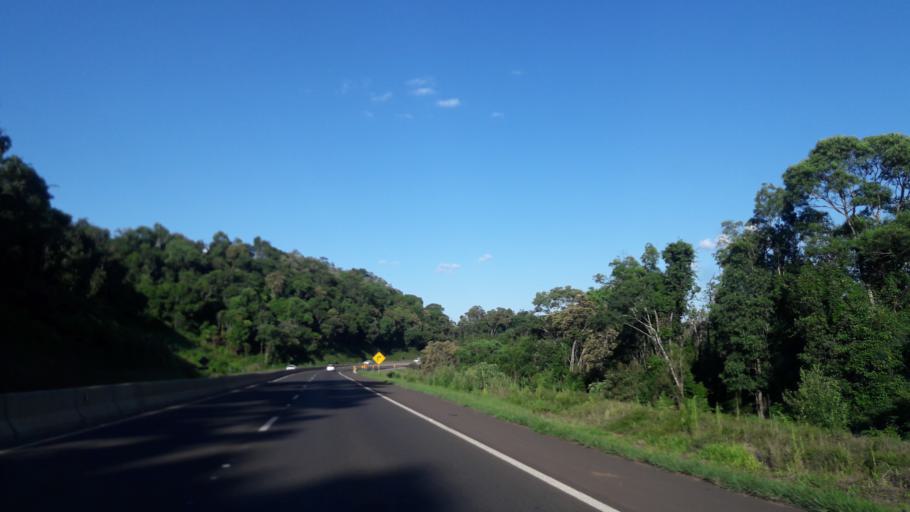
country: BR
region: Parana
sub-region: Guarapuava
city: Guarapuava
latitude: -25.3470
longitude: -51.3873
